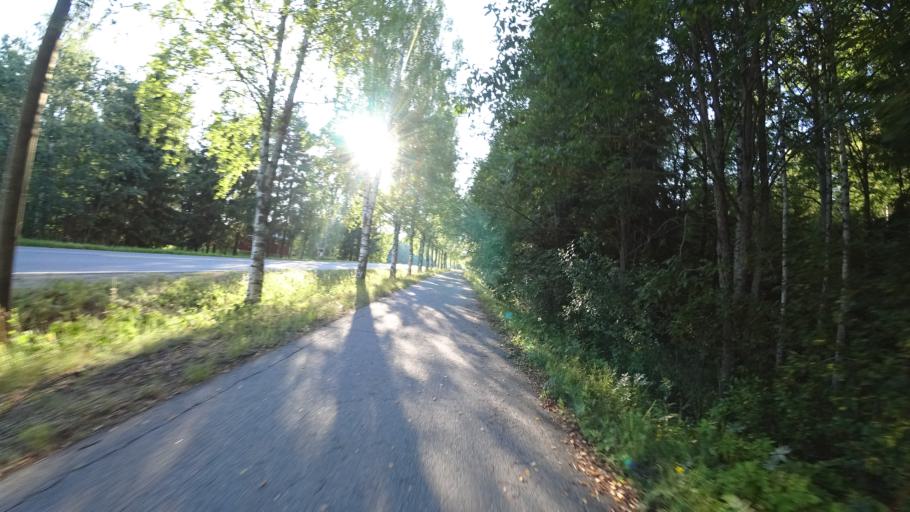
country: FI
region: Pirkanmaa
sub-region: Tampere
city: Nokia
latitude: 61.4709
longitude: 23.3873
